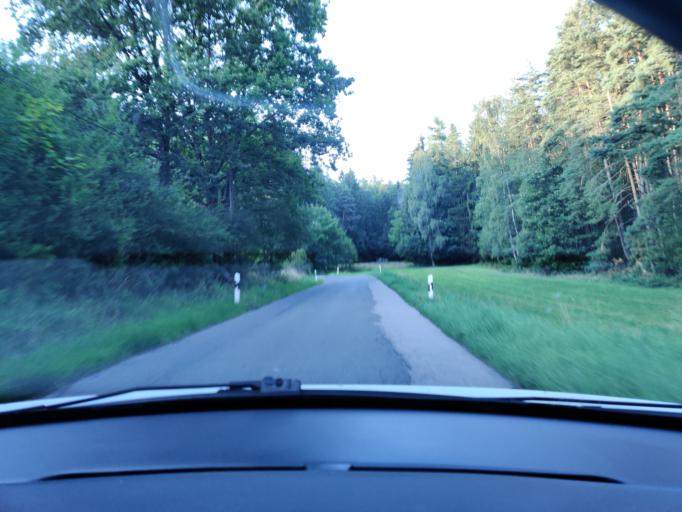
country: DE
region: Bavaria
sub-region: Upper Palatinate
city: Nabburg
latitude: 49.4170
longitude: 12.1777
